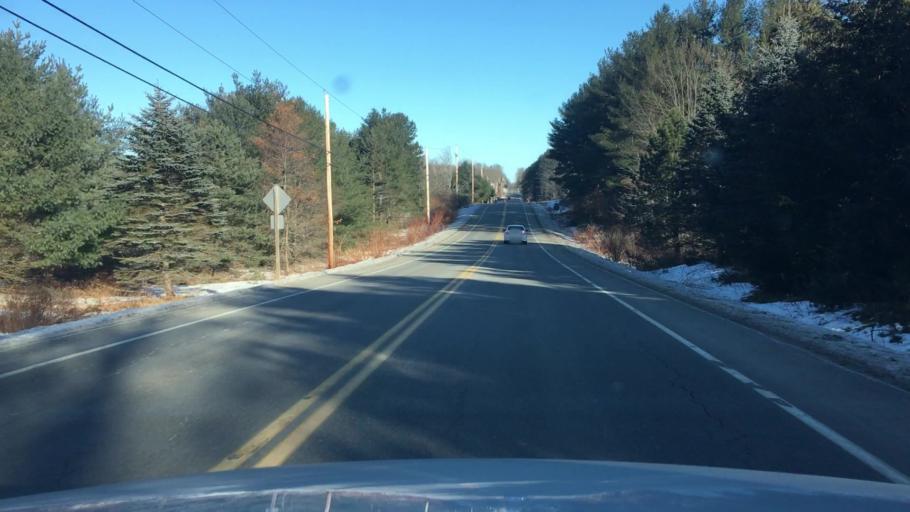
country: US
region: Maine
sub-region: Cumberland County
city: Freeport
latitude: 43.9025
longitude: -70.1164
